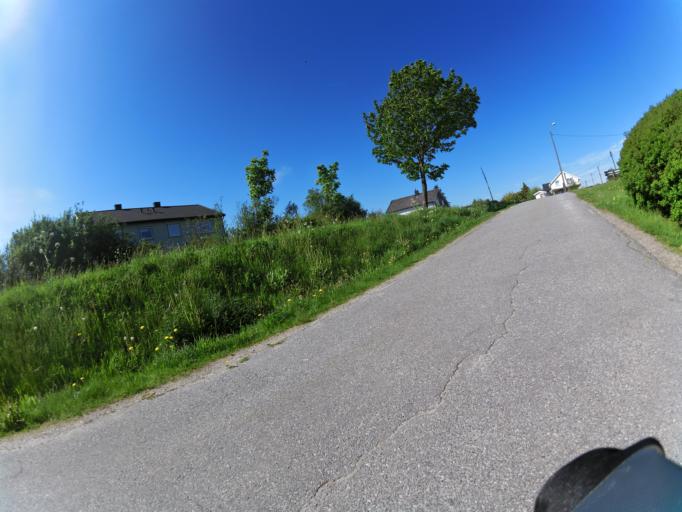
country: NO
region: Ostfold
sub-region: Fredrikstad
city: Fredrikstad
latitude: 59.2313
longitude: 11.0007
